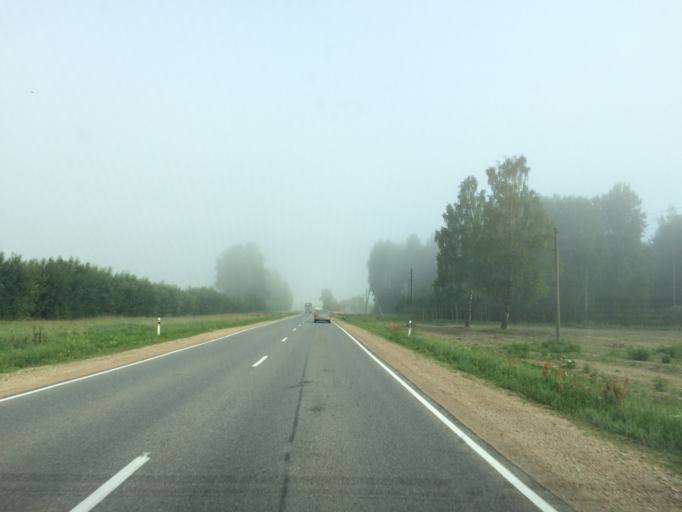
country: LV
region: Salas
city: Sala
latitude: 56.5615
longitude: 25.7788
